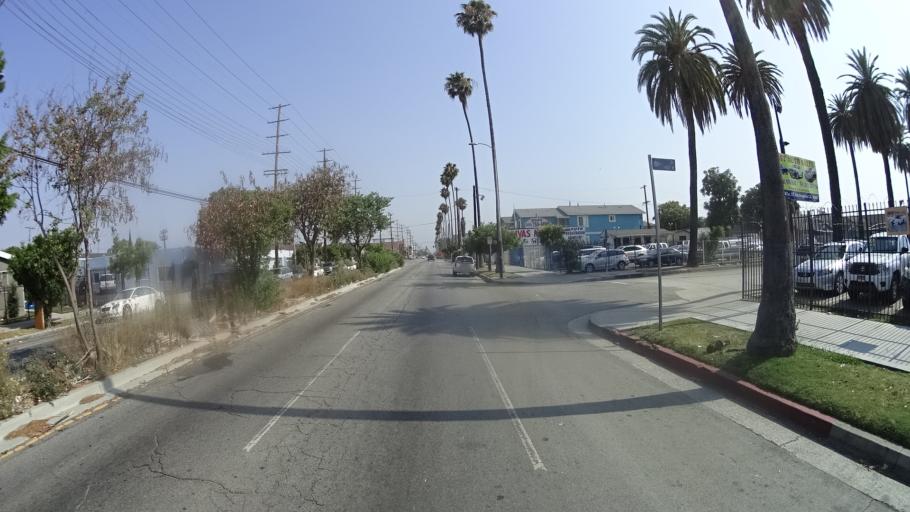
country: US
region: California
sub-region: Los Angeles County
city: Westmont
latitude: 33.9658
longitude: -118.2827
